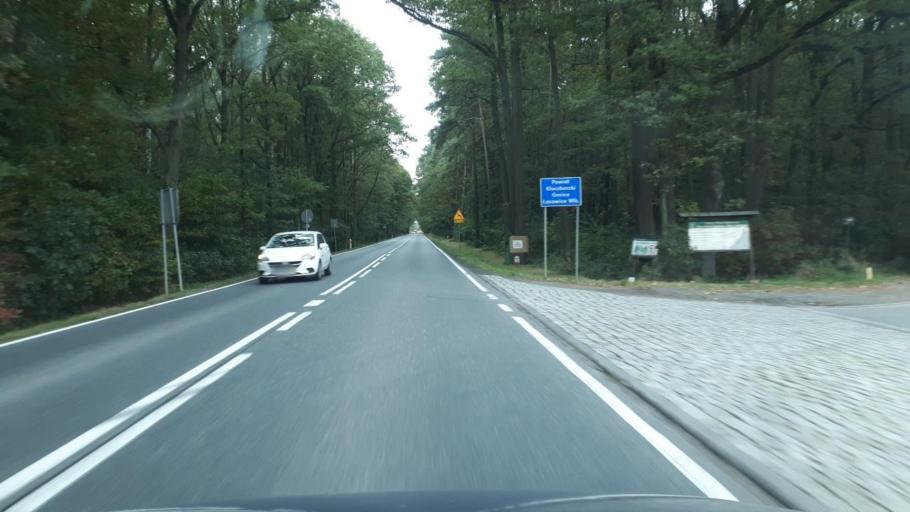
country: PL
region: Opole Voivodeship
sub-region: Powiat oleski
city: Olesno
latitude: 50.9221
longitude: 18.3387
